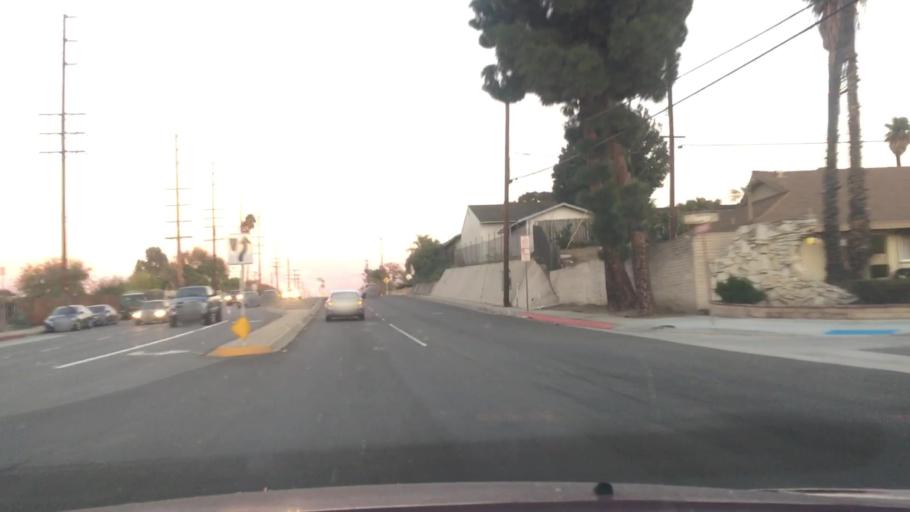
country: US
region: California
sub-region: Los Angeles County
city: La Mirada
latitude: 33.9274
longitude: -118.0092
